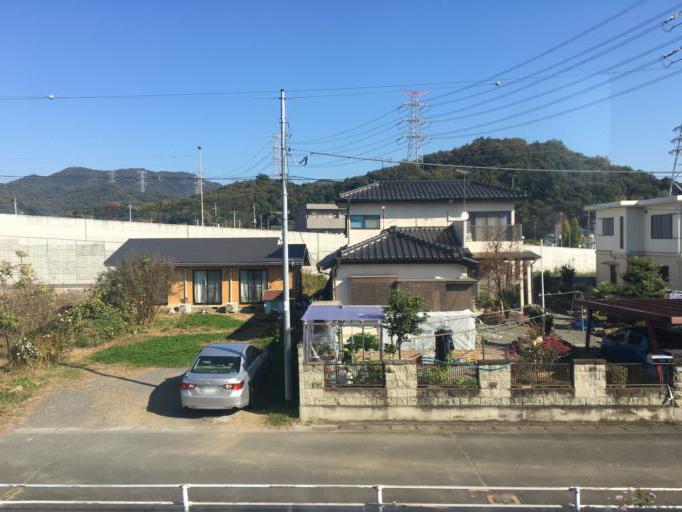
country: JP
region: Gunma
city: Kiryu
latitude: 36.3707
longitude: 139.3800
